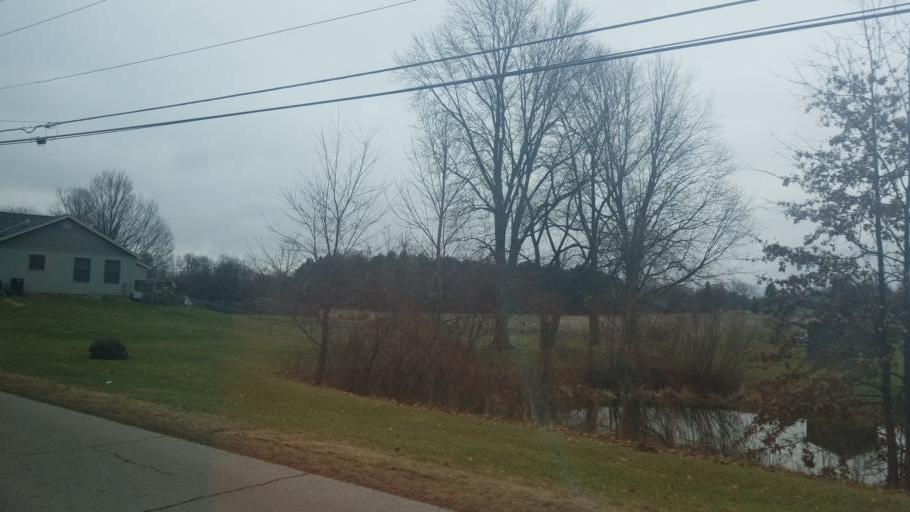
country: US
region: Ohio
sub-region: Crawford County
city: Galion
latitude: 40.7536
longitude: -82.7878
